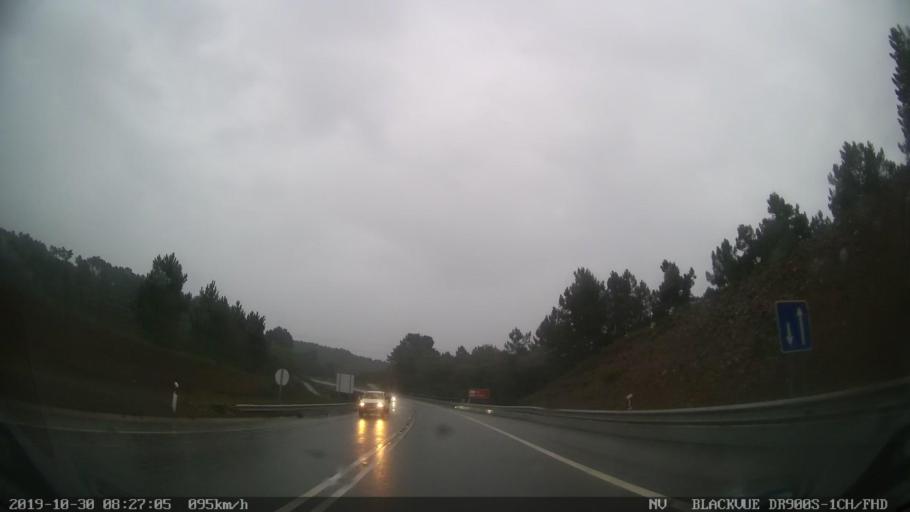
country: PT
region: Vila Real
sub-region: Sabrosa
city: Vilela
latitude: 41.2642
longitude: -7.6714
